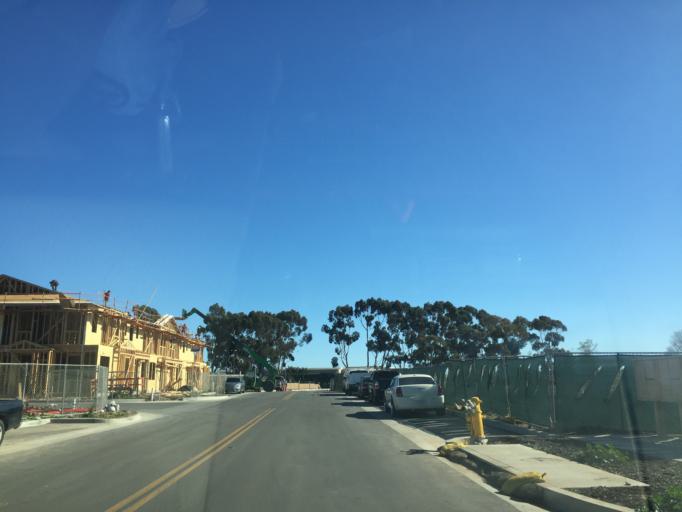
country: US
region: California
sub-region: Santa Barbara County
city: Isla Vista
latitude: 34.4342
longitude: -119.8595
